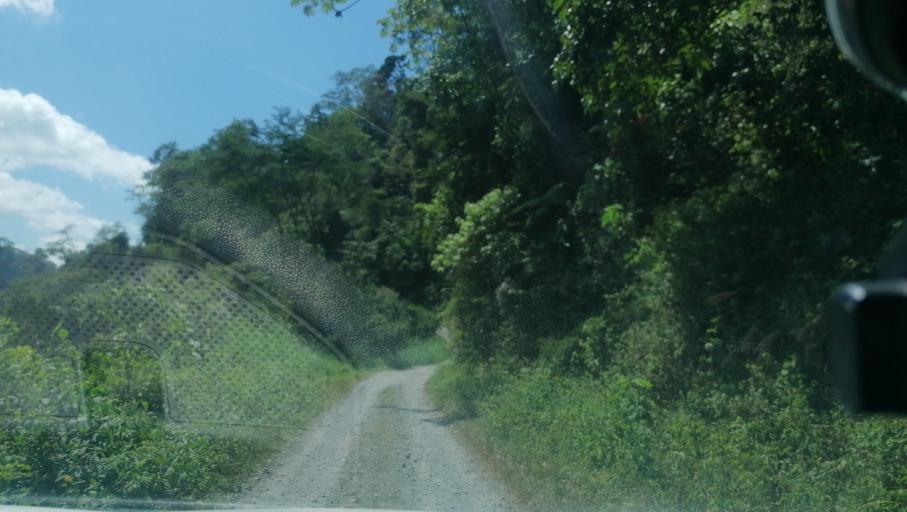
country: MX
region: Chiapas
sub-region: Union Juarez
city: Santo Domingo
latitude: 15.0687
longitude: -92.1375
